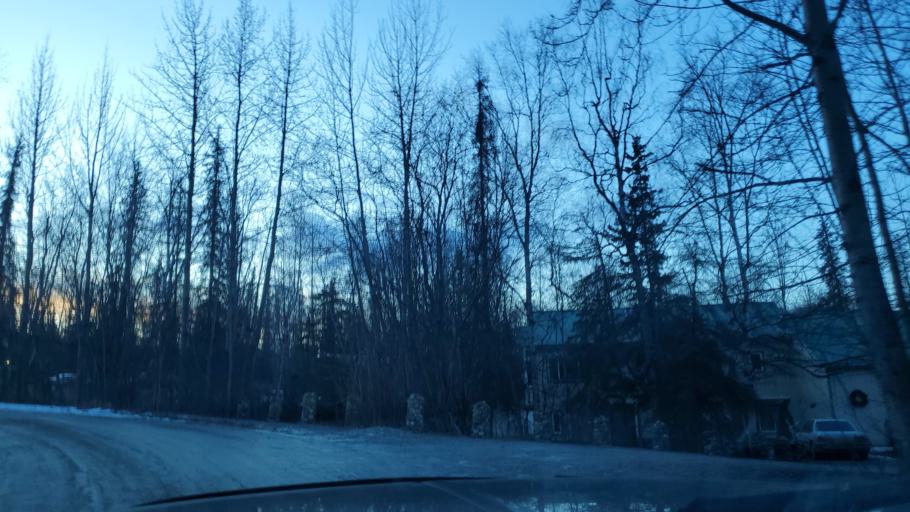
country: US
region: Alaska
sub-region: Matanuska-Susitna Borough
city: Tanaina
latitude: 61.6126
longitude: -149.4037
